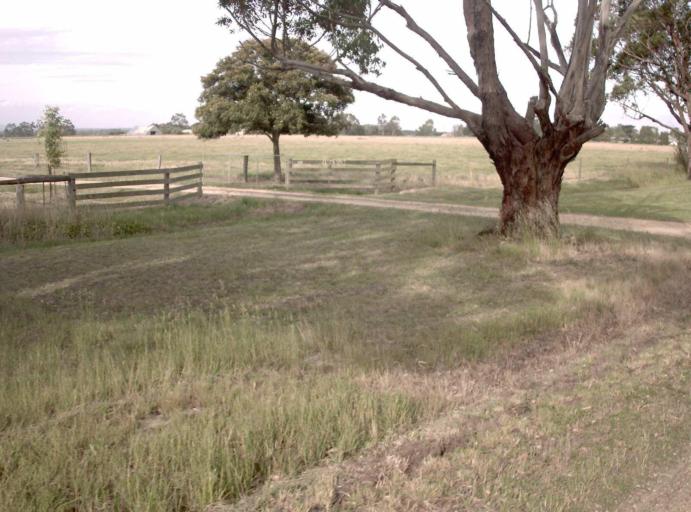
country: AU
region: Victoria
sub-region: Wellington
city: Heyfield
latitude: -38.0134
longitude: 146.6891
